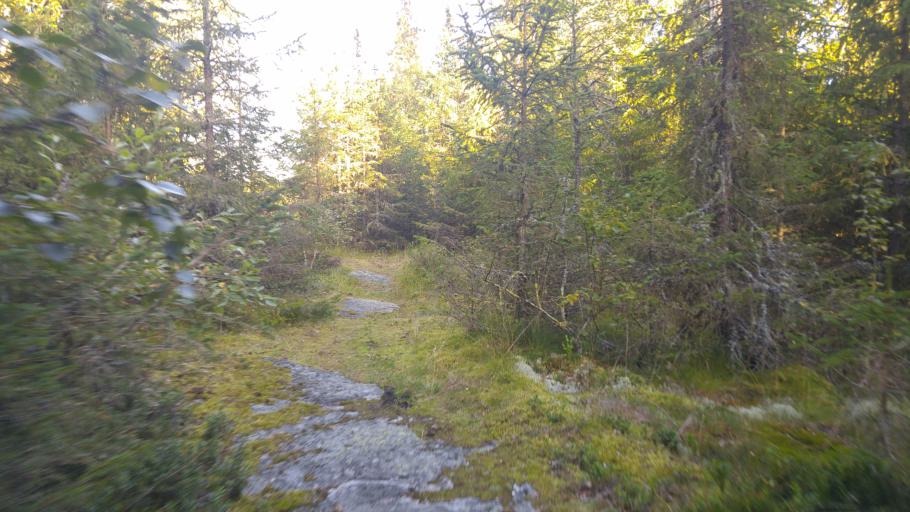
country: NO
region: Buskerud
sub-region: Hemsedal
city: Troim
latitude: 60.8509
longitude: 8.6124
